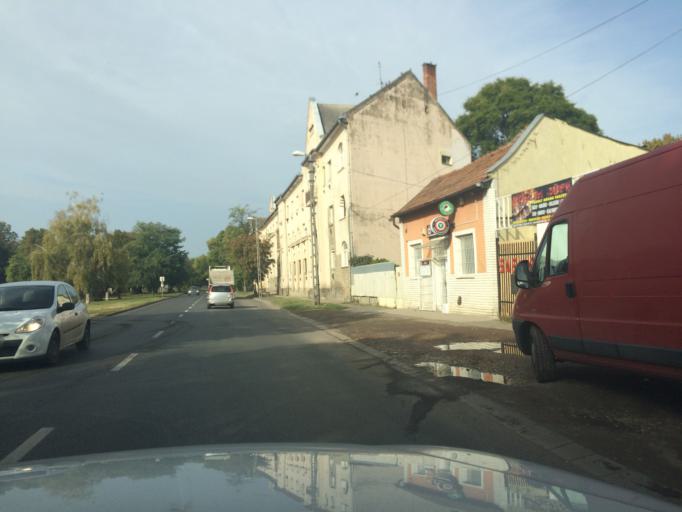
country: HU
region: Szabolcs-Szatmar-Bereg
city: Nyiregyhaza
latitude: 47.9416
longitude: 21.7124
